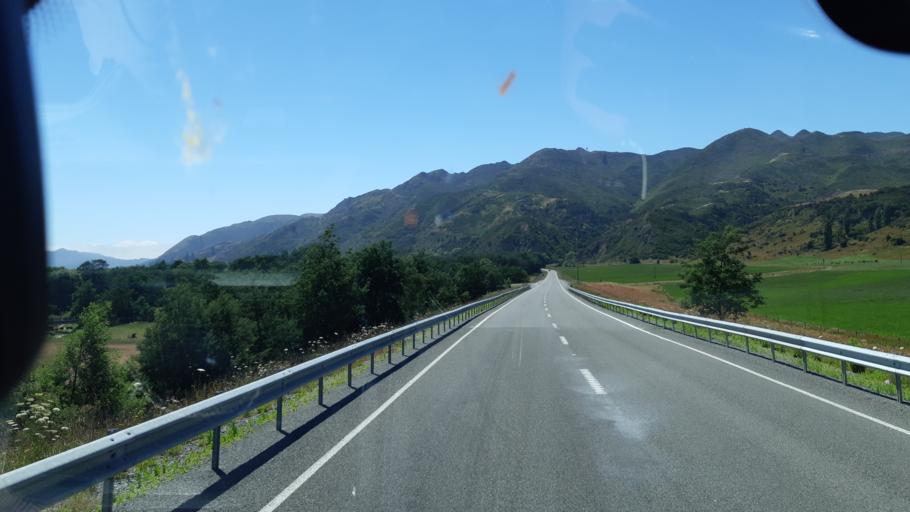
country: NZ
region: Canterbury
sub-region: Kaikoura District
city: Kaikoura
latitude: -42.6366
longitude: 173.3314
